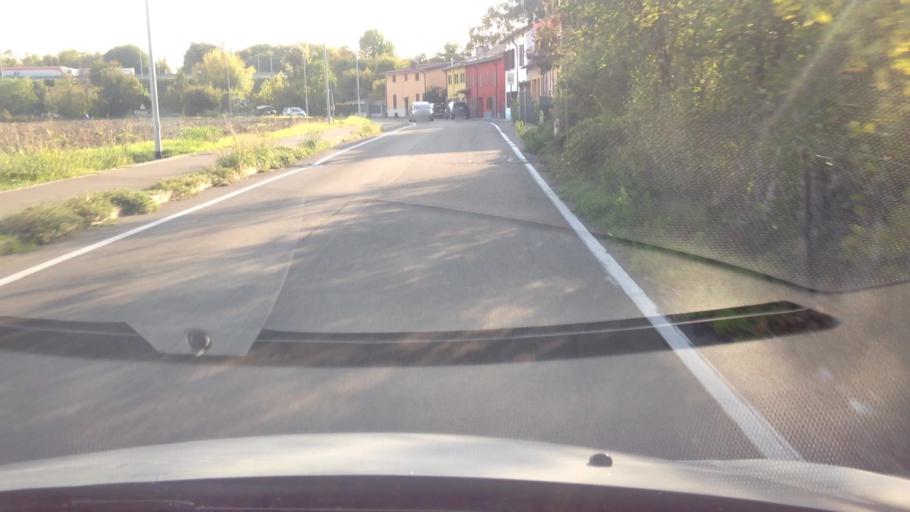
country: IT
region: Emilia-Romagna
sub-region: Provincia di Modena
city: Baggiovara
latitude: 44.6194
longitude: 10.8897
